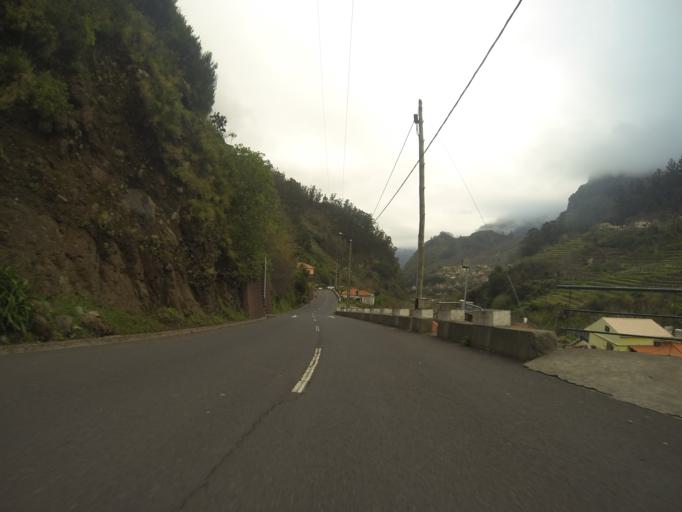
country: PT
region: Madeira
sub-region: Camara de Lobos
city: Curral das Freiras
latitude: 32.7344
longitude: -16.9687
